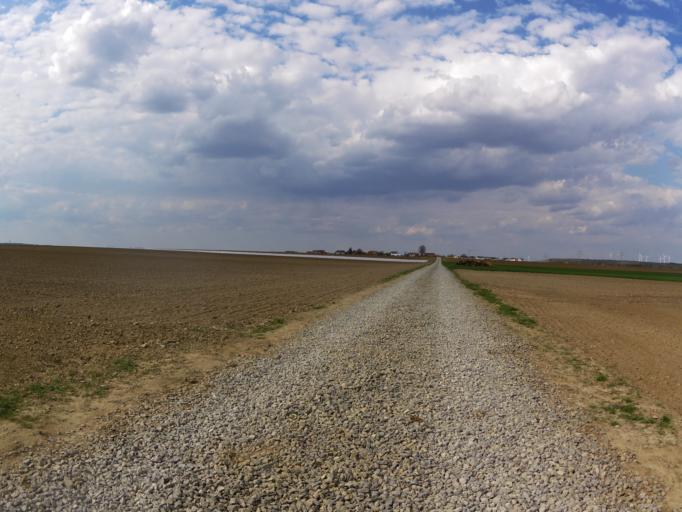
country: DE
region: Bavaria
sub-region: Regierungsbezirk Unterfranken
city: Oberpleichfeld
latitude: 49.8662
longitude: 10.0934
